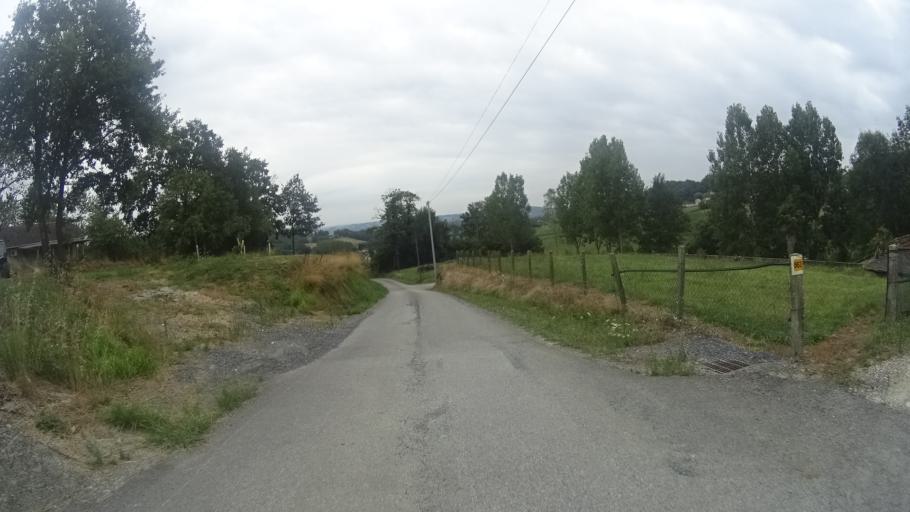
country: FR
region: Aquitaine
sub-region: Departement des Pyrenees-Atlantiques
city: Mont
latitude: 43.4929
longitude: -0.6931
